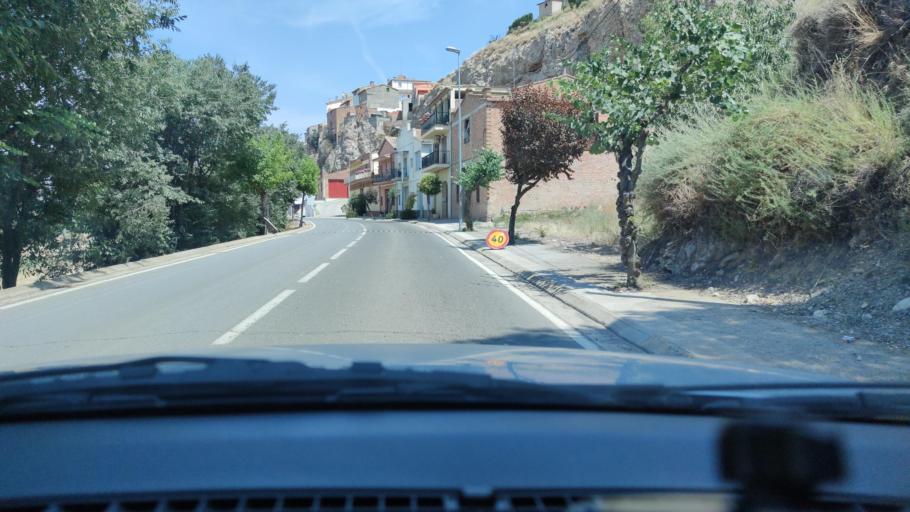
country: ES
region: Catalonia
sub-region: Provincia de Lleida
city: Alfarras
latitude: 41.8480
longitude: 0.5853
